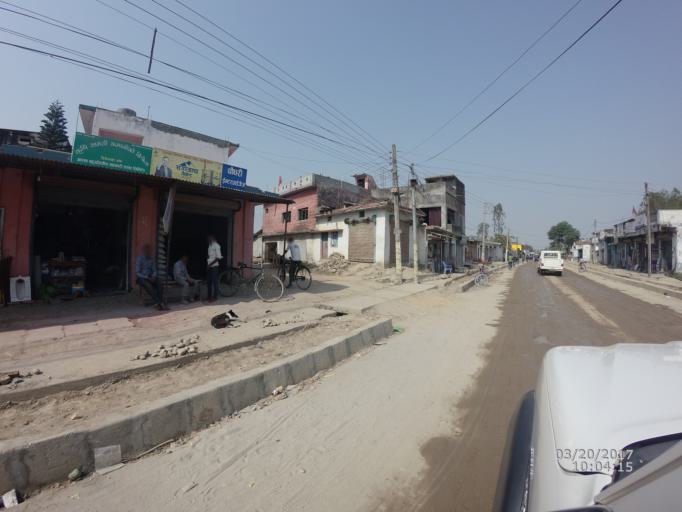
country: NP
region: Mid Western
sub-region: Bheri Zone
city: Nepalgunj
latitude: 28.1001
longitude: 81.6562
